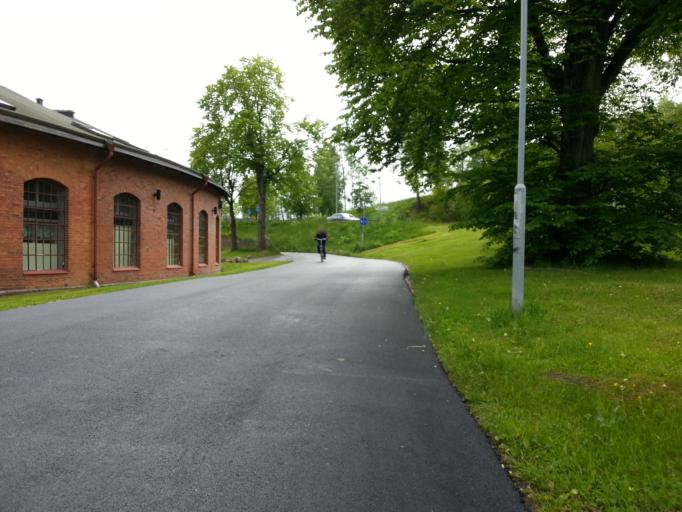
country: SE
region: Joenkoeping
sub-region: Jonkopings Kommun
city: Jonkoping
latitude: 57.7879
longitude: 14.1505
